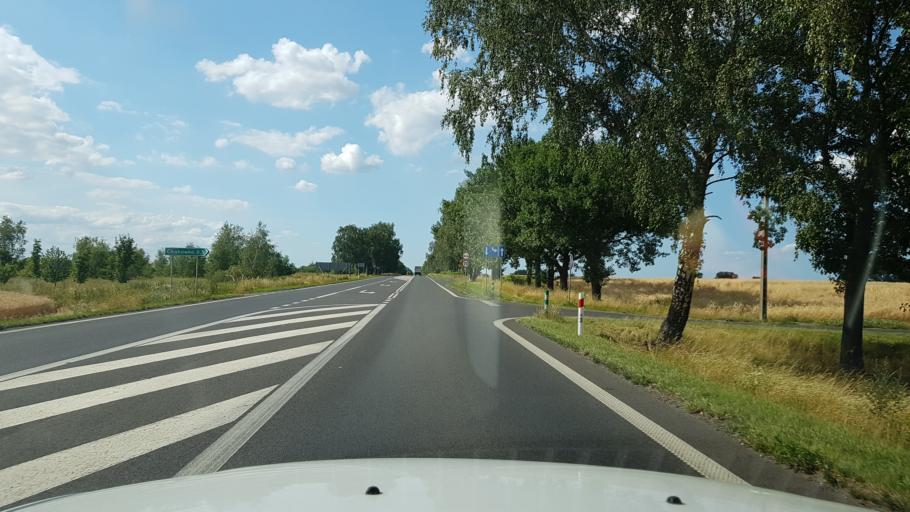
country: PL
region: West Pomeranian Voivodeship
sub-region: Powiat gryfinski
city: Stare Czarnowo
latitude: 53.2297
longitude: 14.7928
